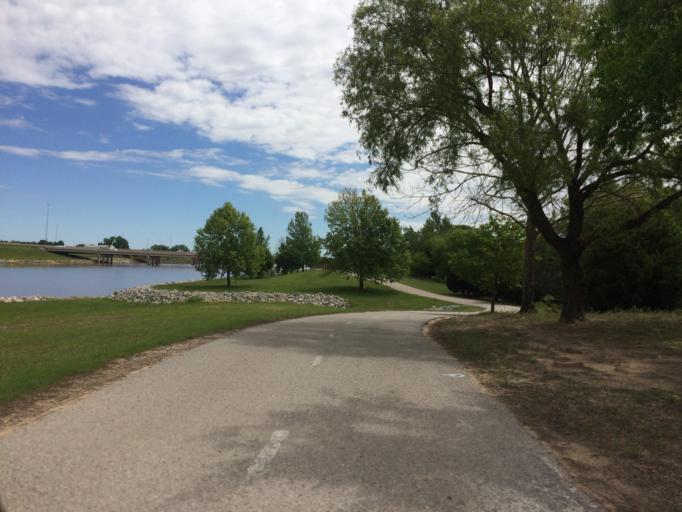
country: US
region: Oklahoma
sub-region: Oklahoma County
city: Oklahoma City
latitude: 35.4573
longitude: -97.4967
